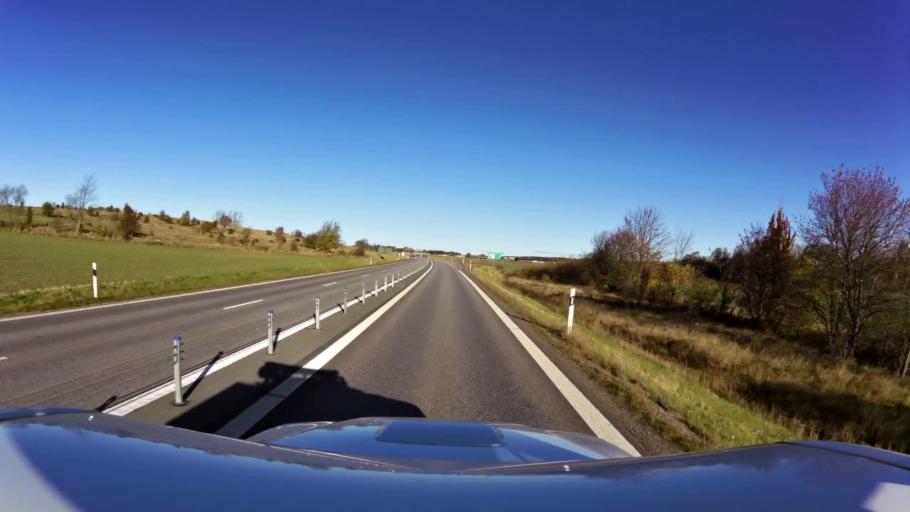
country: SE
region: OEstergoetland
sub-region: Linkopings Kommun
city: Berg
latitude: 58.4746
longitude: 15.4899
